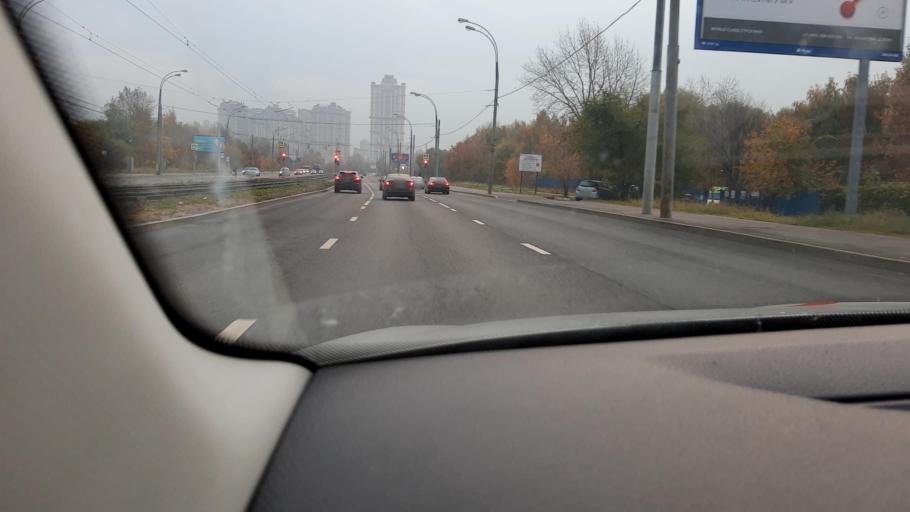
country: RU
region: Moscow
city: Strogino
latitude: 55.8035
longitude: 37.4276
